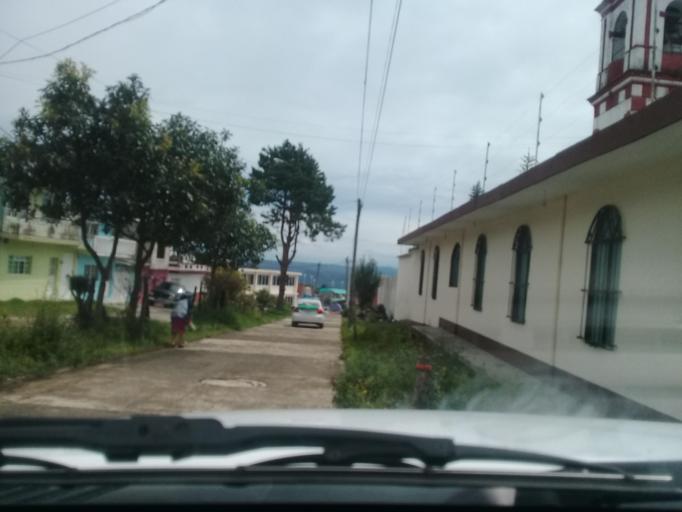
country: MX
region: Veracruz
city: Rafael Lucio
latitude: 19.5923
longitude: -96.9914
